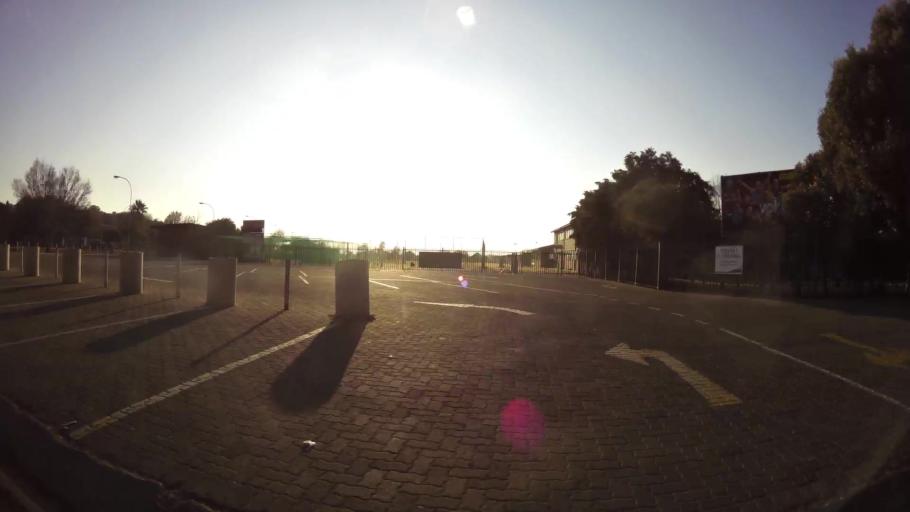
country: ZA
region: Orange Free State
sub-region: Mangaung Metropolitan Municipality
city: Bloemfontein
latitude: -29.1474
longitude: 26.1665
